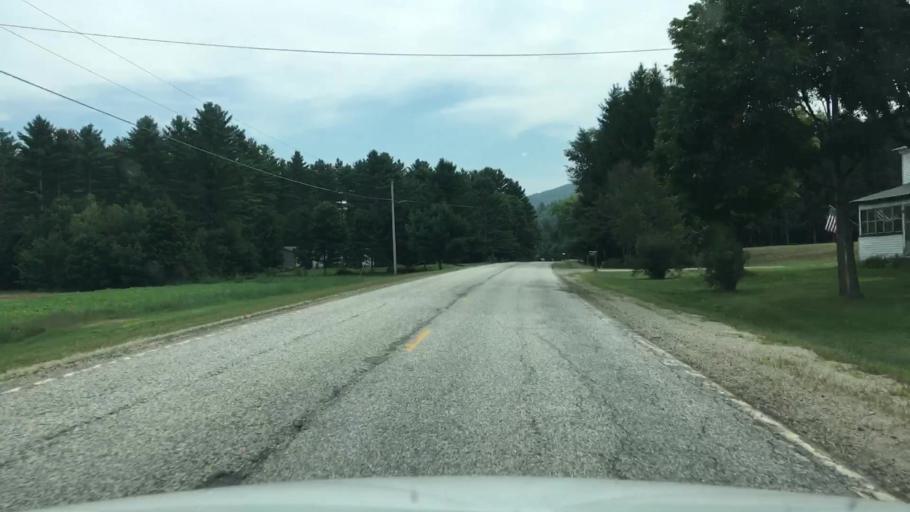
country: US
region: Maine
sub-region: Oxford County
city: Rumford
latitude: 44.5850
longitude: -70.7344
